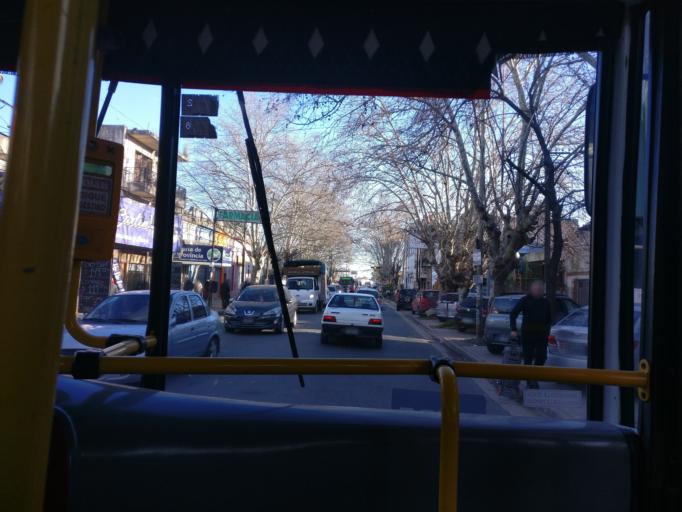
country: AR
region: Buenos Aires
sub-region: Partido de Ezeiza
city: Ezeiza
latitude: -34.8899
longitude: -58.5679
